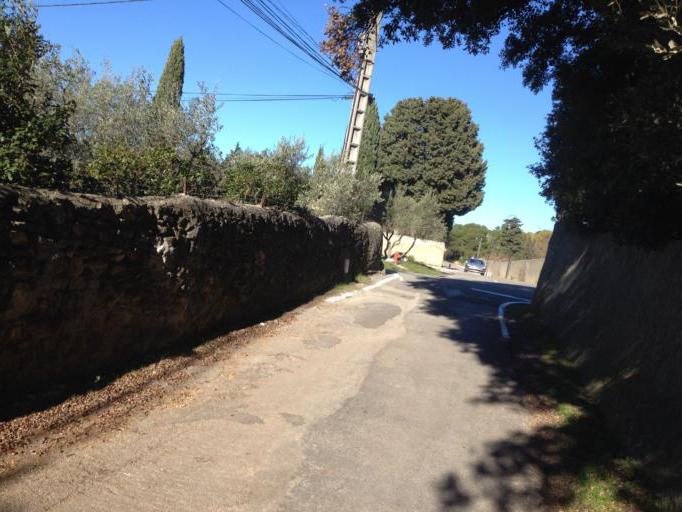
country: FR
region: Provence-Alpes-Cote d'Azur
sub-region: Departement du Vaucluse
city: Orange
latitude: 44.1298
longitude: 4.8096
